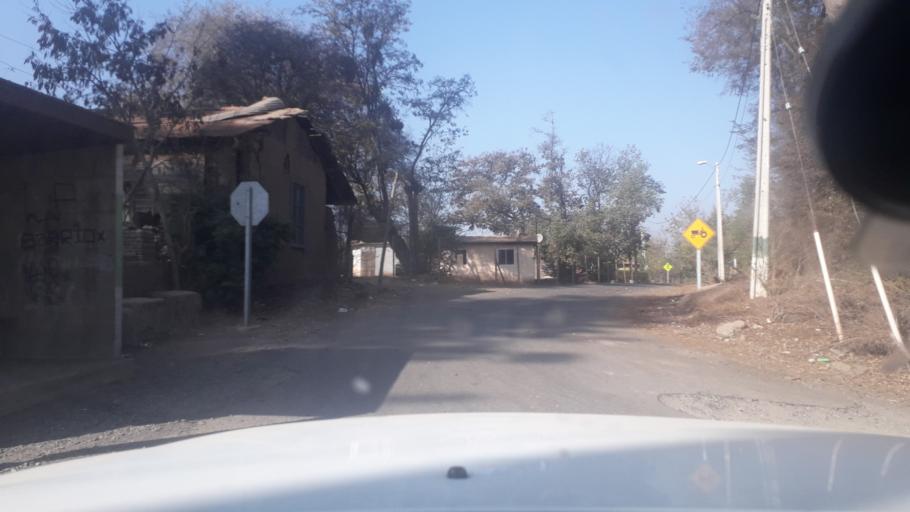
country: CL
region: Valparaiso
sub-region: Provincia de San Felipe
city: Llaillay
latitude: -32.8197
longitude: -71.0272
